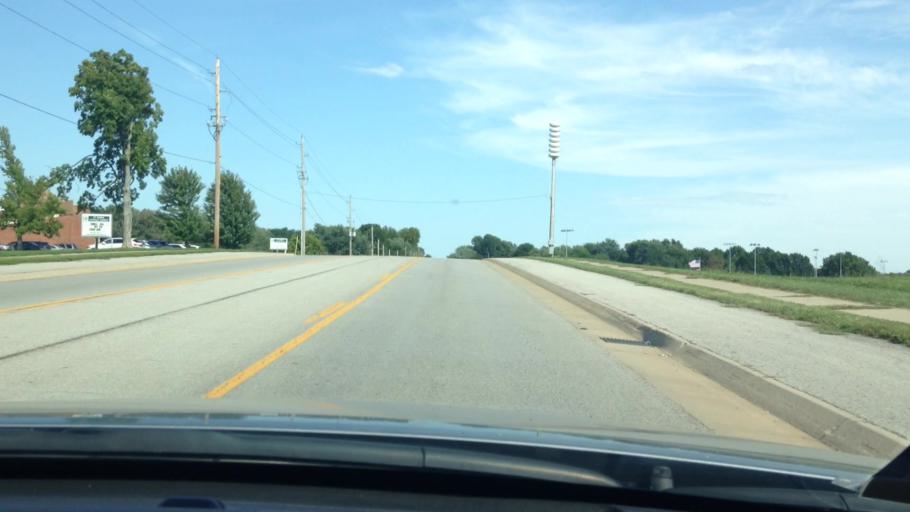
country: US
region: Missouri
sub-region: Cass County
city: Belton
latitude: 38.8158
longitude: -94.5532
